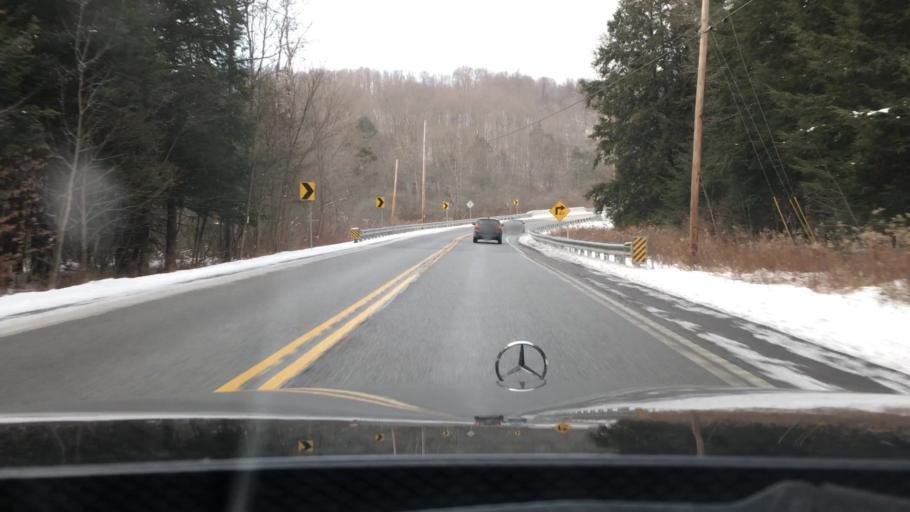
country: US
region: Pennsylvania
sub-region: Cambria County
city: Gallitzin
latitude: 40.5121
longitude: -78.5833
